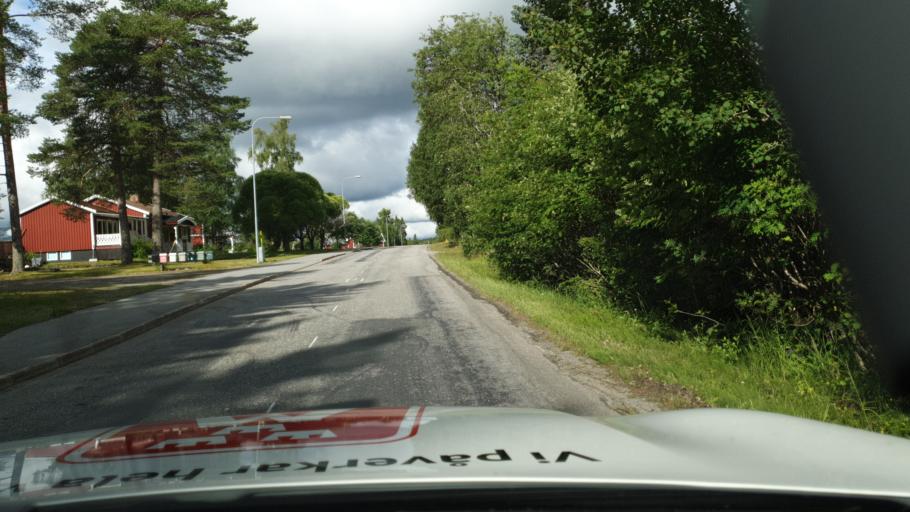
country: SE
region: Vaesterbotten
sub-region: Umea Kommun
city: Hoernefors
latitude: 63.6806
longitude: 20.0121
